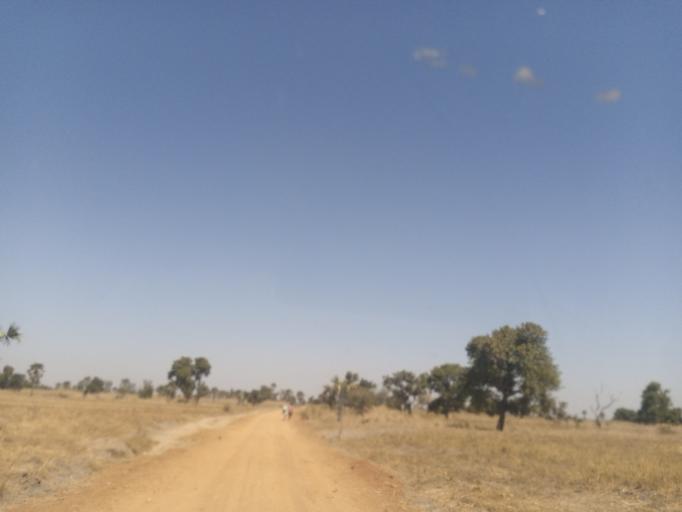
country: NG
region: Adamawa
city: Yola
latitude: 9.2937
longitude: 12.8860
